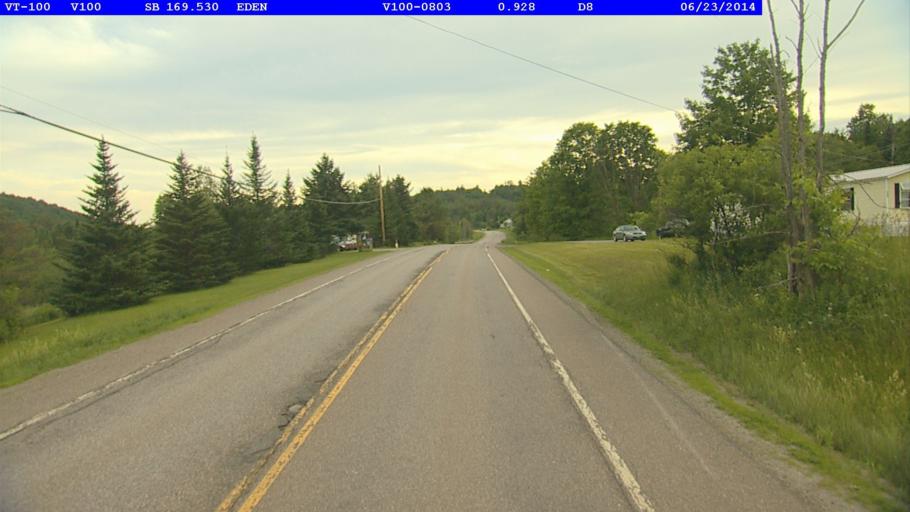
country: US
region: Vermont
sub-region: Lamoille County
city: Hyde Park
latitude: 44.6946
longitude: -72.5808
